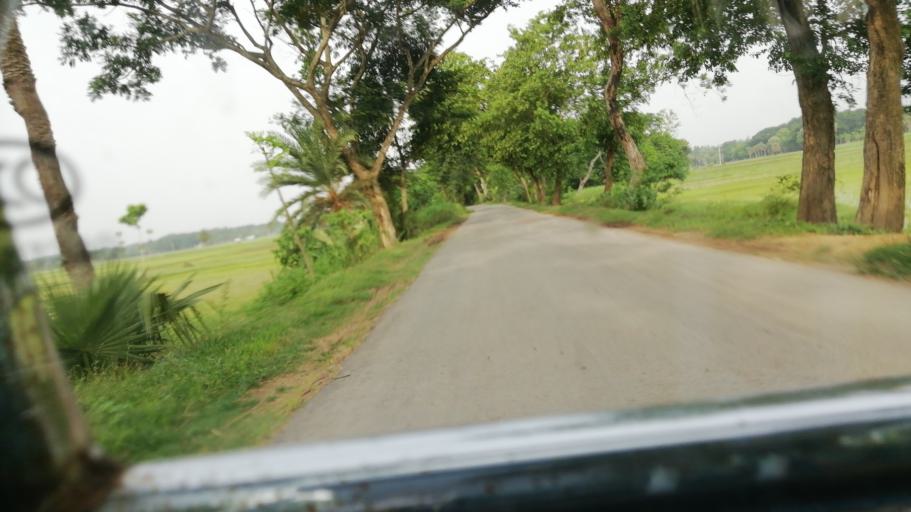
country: BD
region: Khulna
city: Kesabpur
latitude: 23.0351
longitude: 89.2850
